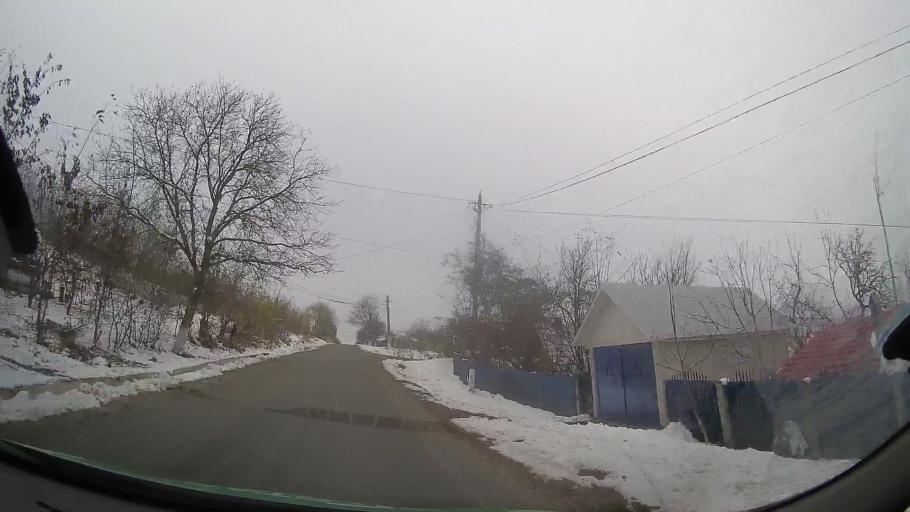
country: RO
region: Bacau
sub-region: Comuna Huruesti
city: Huruesti
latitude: 46.3051
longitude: 27.2942
